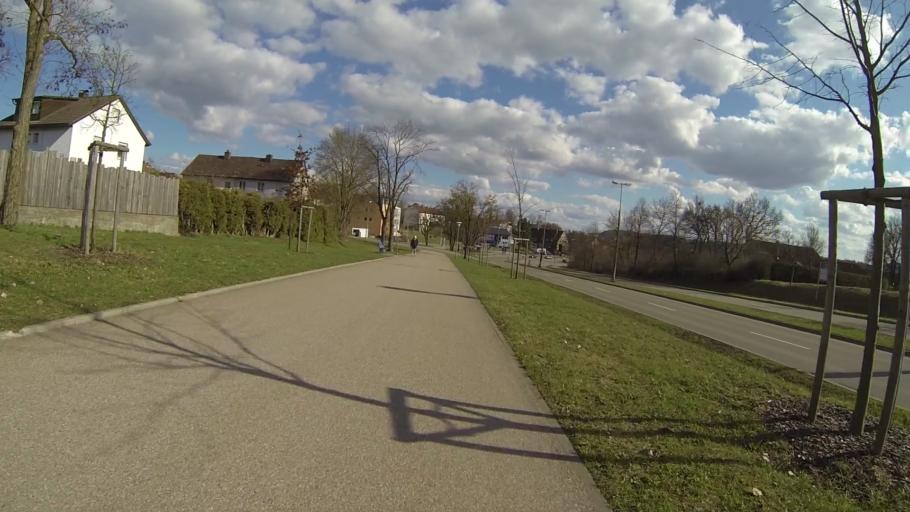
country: DE
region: Baden-Wuerttemberg
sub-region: Regierungsbezirk Stuttgart
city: Heidenheim an der Brenz
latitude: 48.6865
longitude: 10.1450
